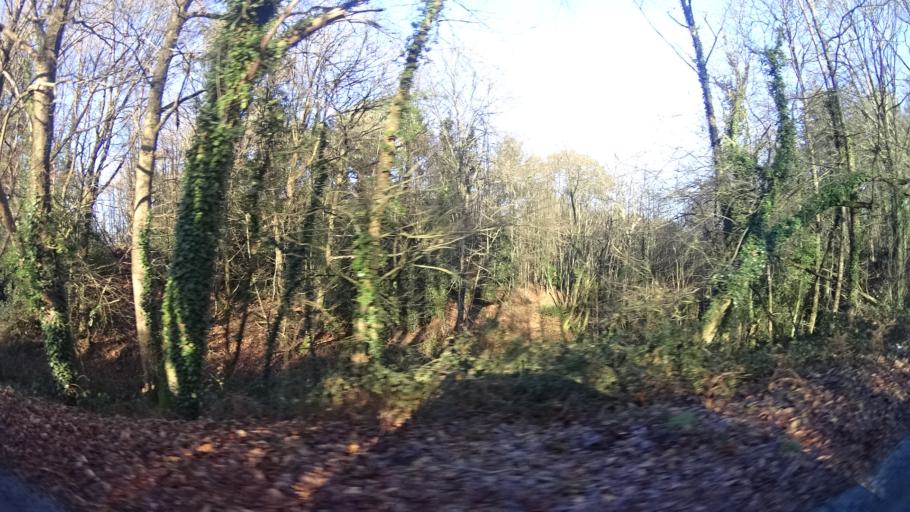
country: FR
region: Brittany
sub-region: Departement du Morbihan
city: Saint-Jacut-les-Pins
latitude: 47.6658
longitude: -2.1917
